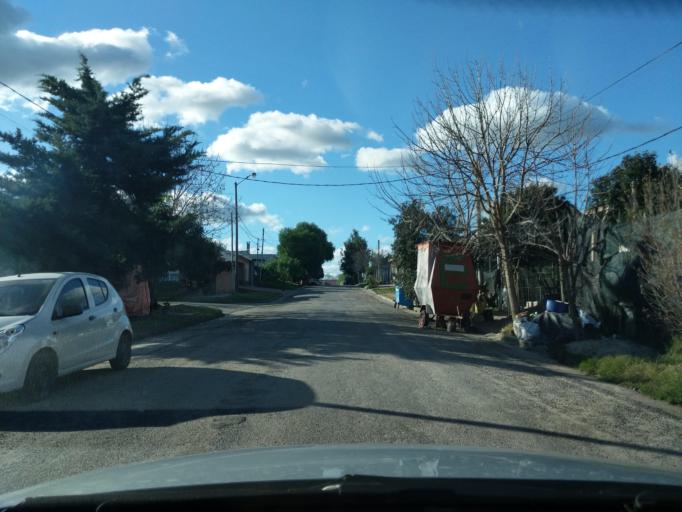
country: UY
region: Florida
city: Florida
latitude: -34.0914
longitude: -56.2108
